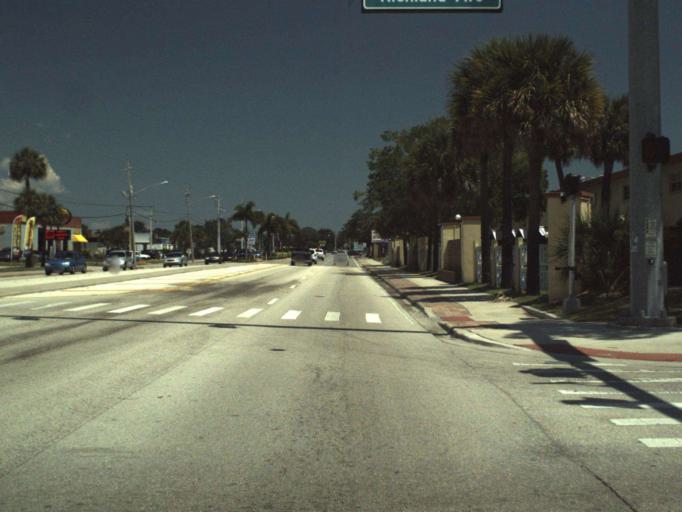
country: US
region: Florida
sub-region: Brevard County
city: Rockledge
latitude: 28.3692
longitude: -80.7002
